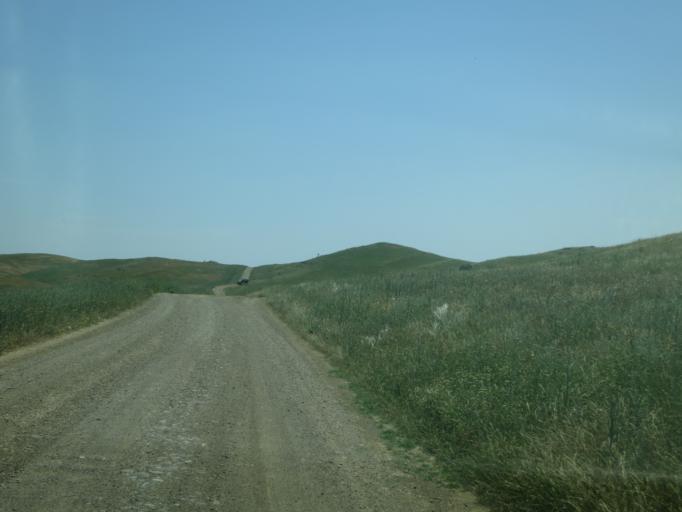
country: AZ
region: Agstafa
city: Saloglu
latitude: 41.4681
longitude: 45.3247
